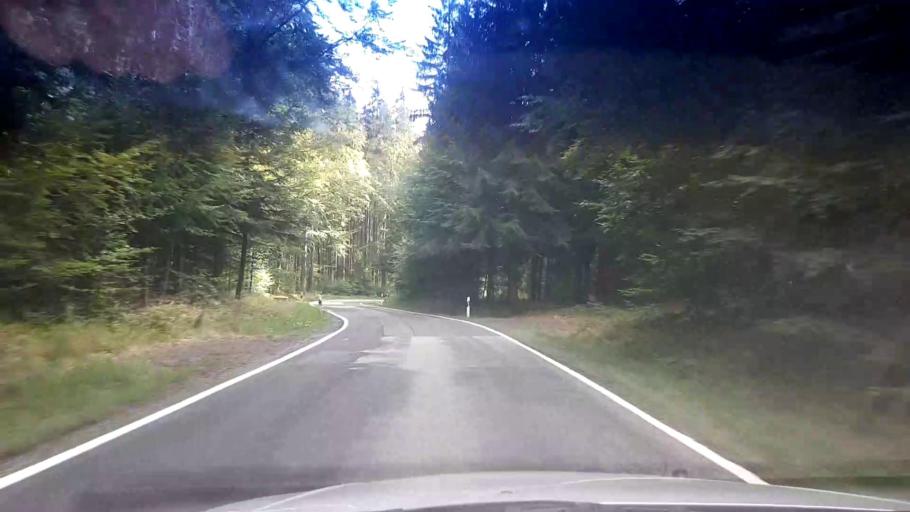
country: DE
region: Bavaria
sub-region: Upper Palatinate
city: Neualbenreuth
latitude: 49.9321
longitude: 12.4084
